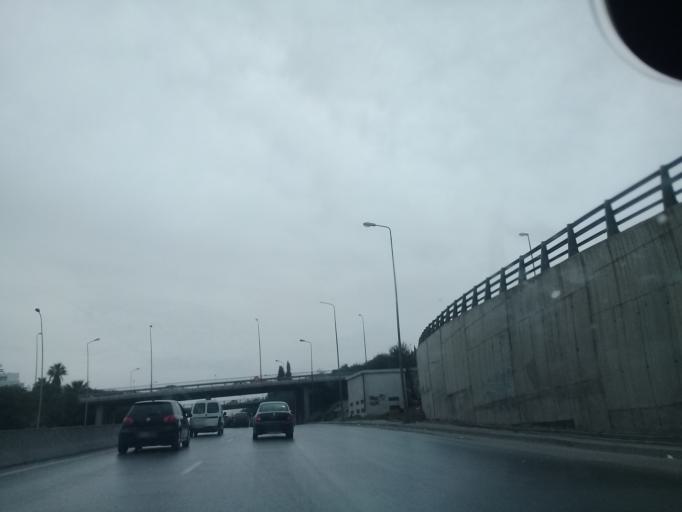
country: TN
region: Tunis
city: Tunis
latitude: 36.8343
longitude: 10.1575
